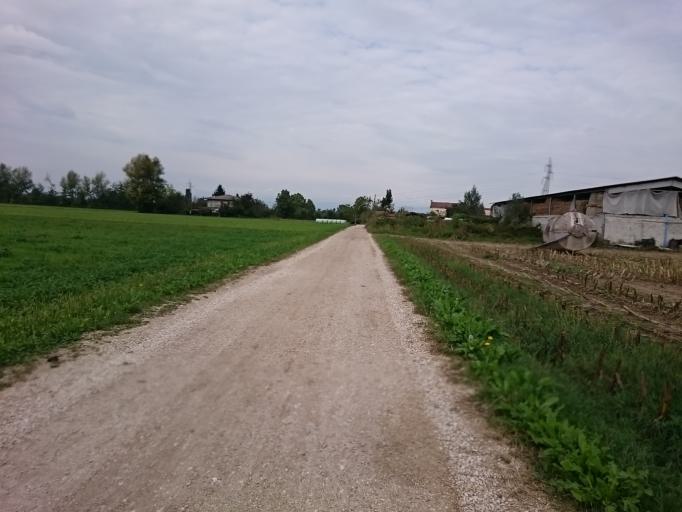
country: IT
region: Veneto
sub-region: Provincia di Vicenza
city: Quinto Vicentino
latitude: 45.5698
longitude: 11.6651
